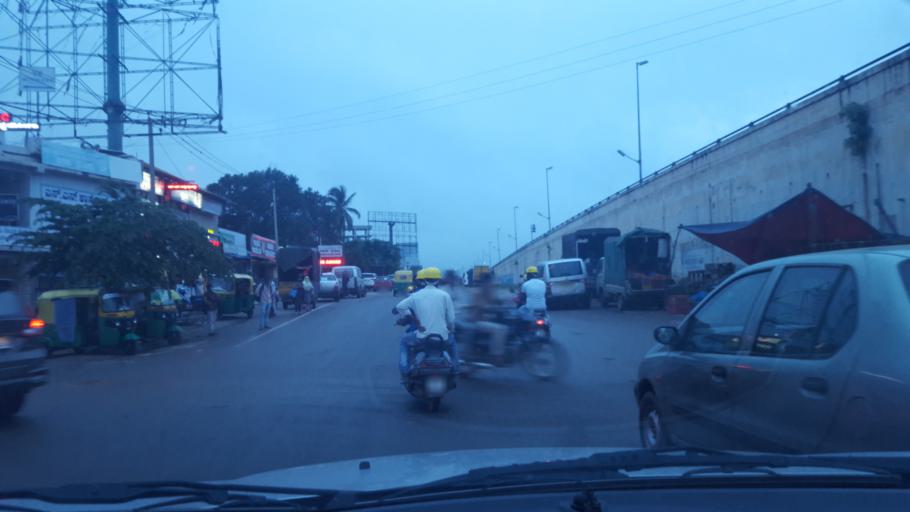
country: IN
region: Karnataka
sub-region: Bangalore Urban
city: Yelahanka
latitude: 13.0979
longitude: 77.5991
